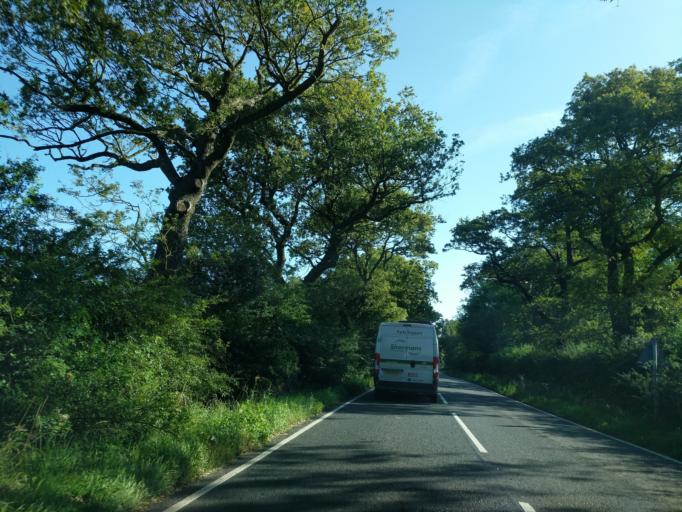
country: GB
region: England
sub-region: Lincolnshire
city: Bourne
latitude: 52.7991
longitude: -0.4673
